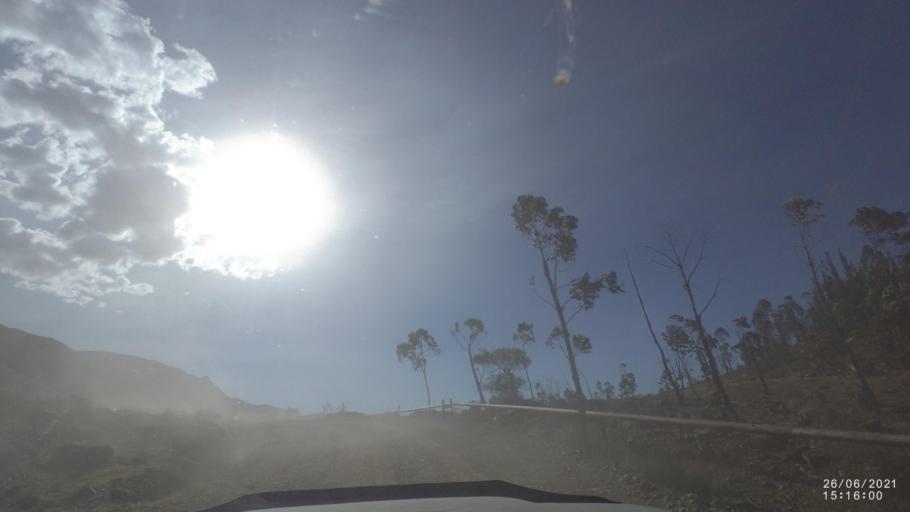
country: BO
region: Cochabamba
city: Mizque
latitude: -17.9562
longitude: -65.6470
